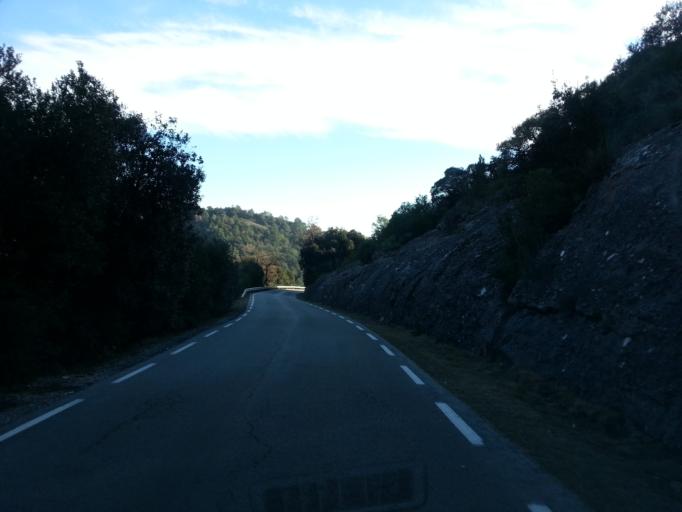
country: ES
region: Catalonia
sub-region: Provincia de Barcelona
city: Mura
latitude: 41.6570
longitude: 1.9831
